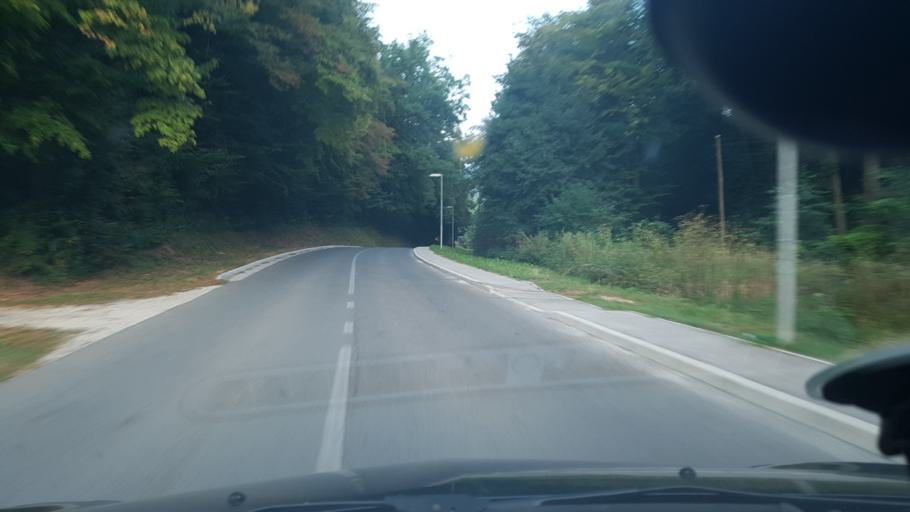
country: SI
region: Rogaska Slatina
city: Rogaska Slatina
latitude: 46.2285
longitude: 15.6617
